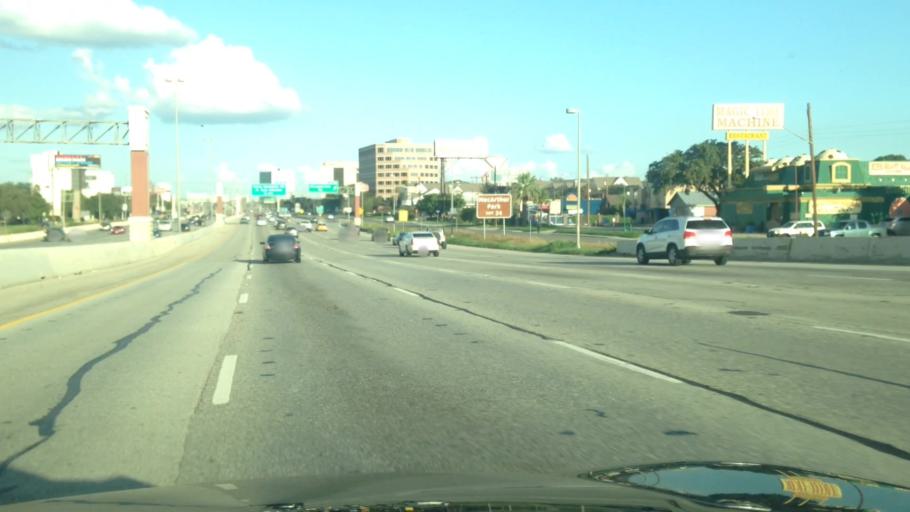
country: US
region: Texas
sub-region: Bexar County
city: Alamo Heights
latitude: 29.5165
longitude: -98.4618
